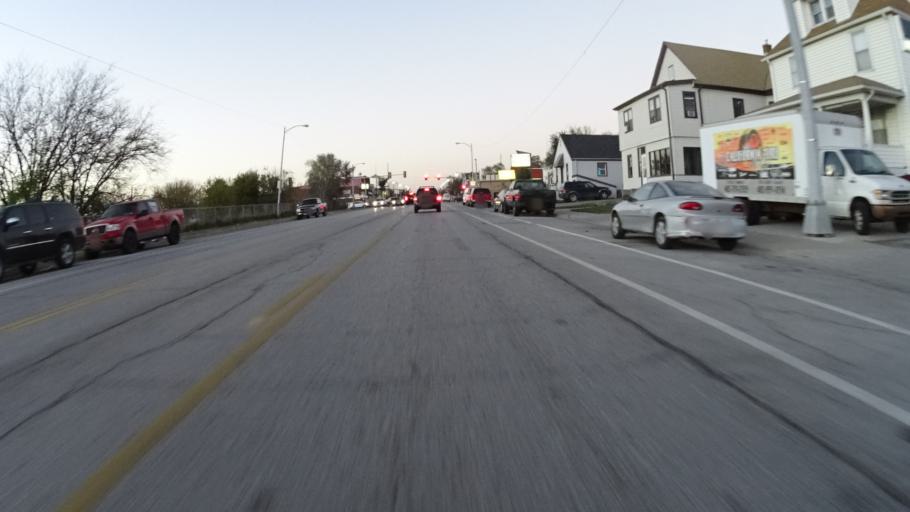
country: US
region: Nebraska
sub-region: Douglas County
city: Omaha
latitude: 41.2044
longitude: -95.9471
